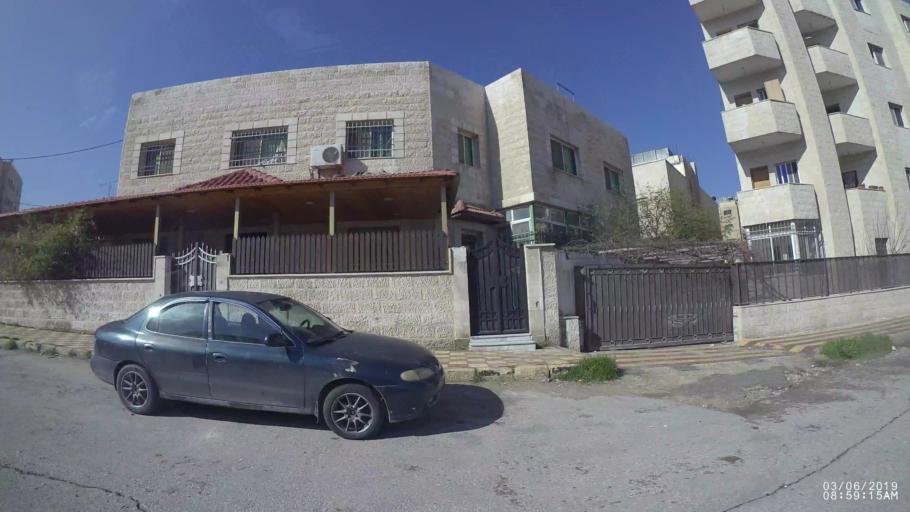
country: JO
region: Zarqa
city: Russeifa
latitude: 31.9917
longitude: 35.9930
